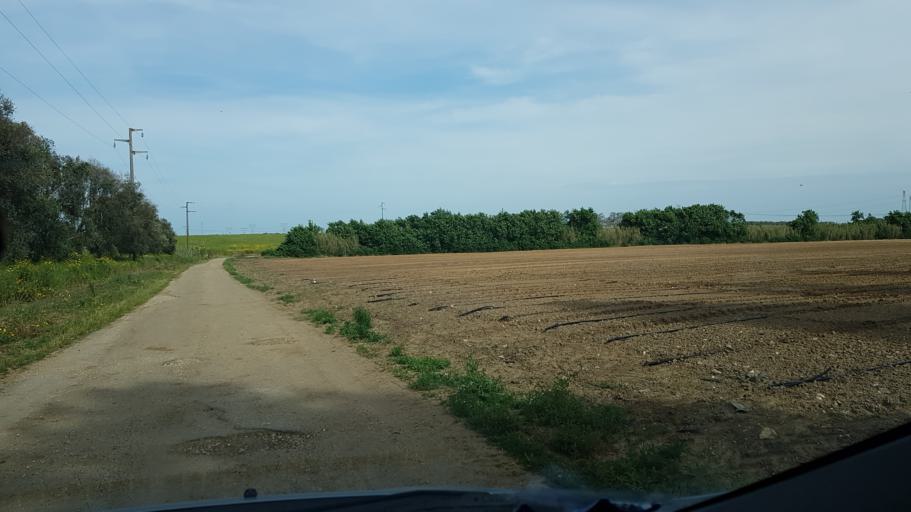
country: IT
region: Apulia
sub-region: Provincia di Brindisi
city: Tuturano
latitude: 40.5612
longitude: 17.9185
